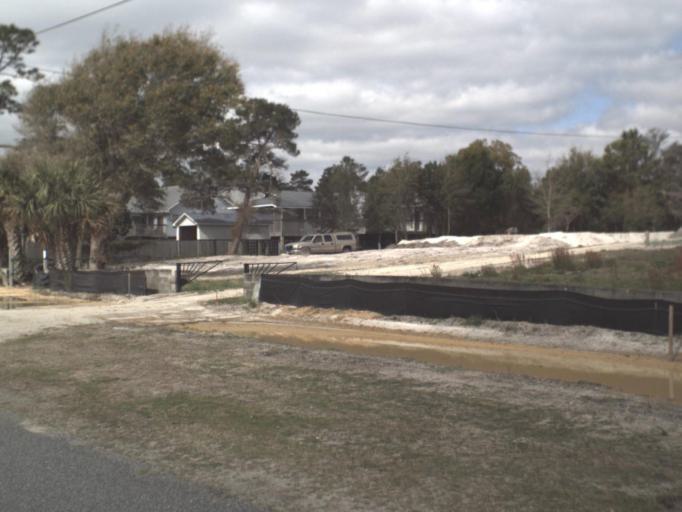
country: US
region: Florida
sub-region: Franklin County
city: Carrabelle
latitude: 29.8289
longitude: -84.6938
